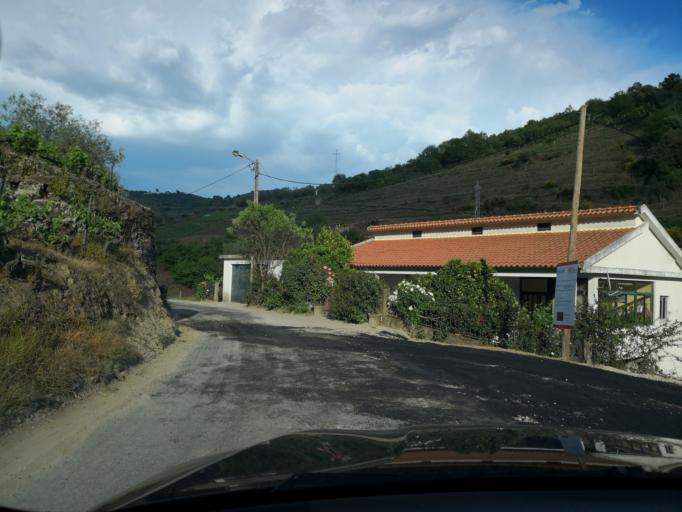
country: PT
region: Vila Real
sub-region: Santa Marta de Penaguiao
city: Santa Marta de Penaguiao
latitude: 41.2196
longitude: -7.7248
